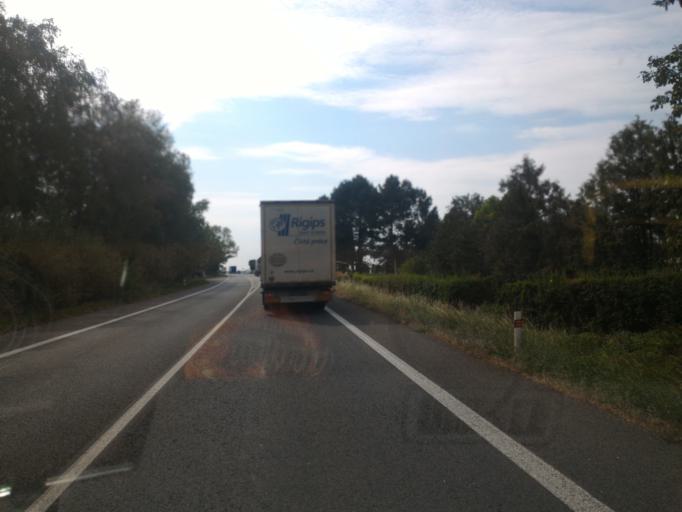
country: CZ
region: Kralovehradecky
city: Horice
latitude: 50.3299
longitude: 15.6336
